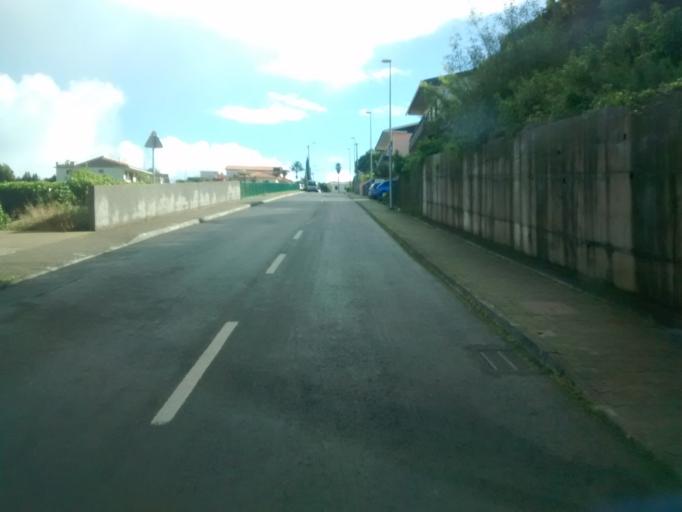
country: PT
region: Madeira
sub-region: Santana
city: Santana
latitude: 32.8050
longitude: -16.8847
